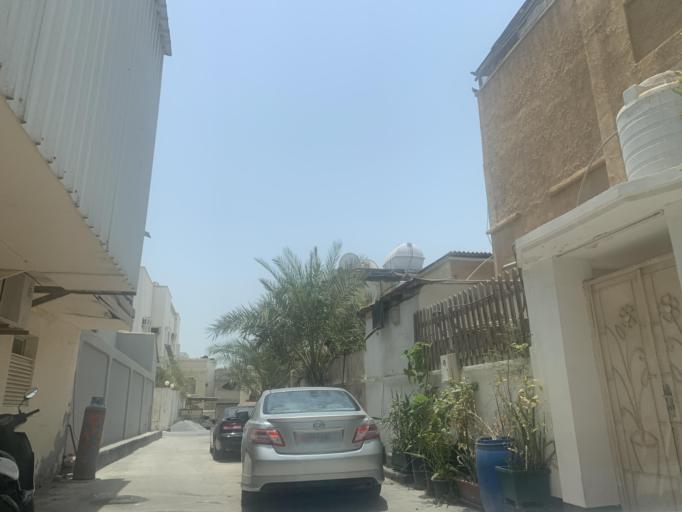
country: BH
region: Manama
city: Jidd Hafs
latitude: 26.2181
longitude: 50.4603
